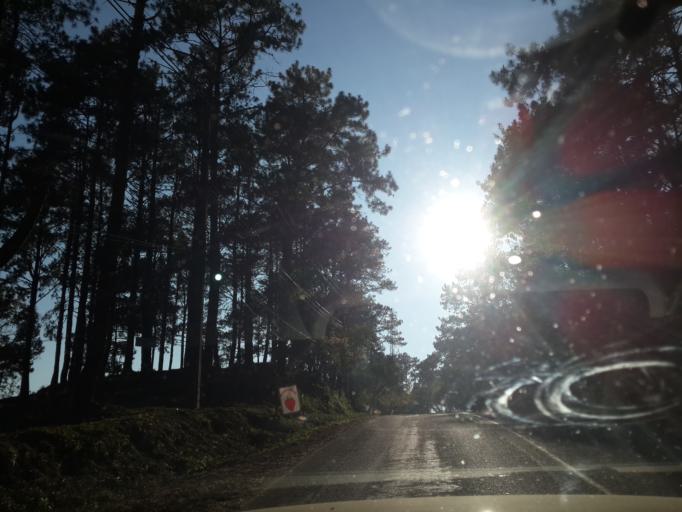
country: TH
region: Chiang Mai
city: Chai Prakan
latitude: 19.8628
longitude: 99.0506
